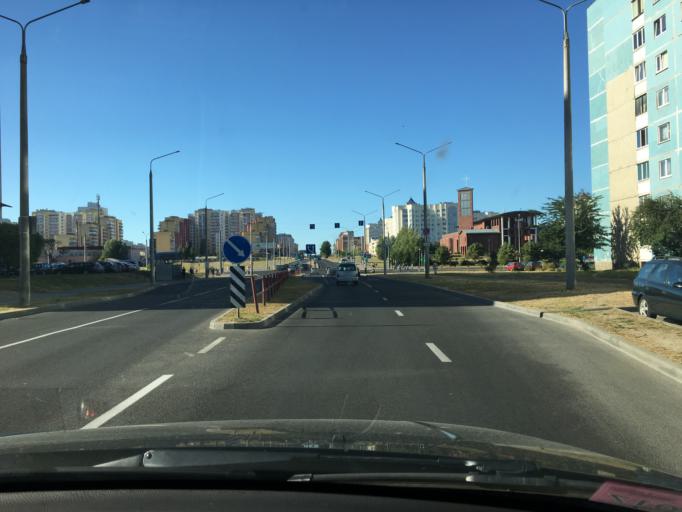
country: BY
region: Grodnenskaya
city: Hrodna
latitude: 53.7058
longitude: 23.8496
